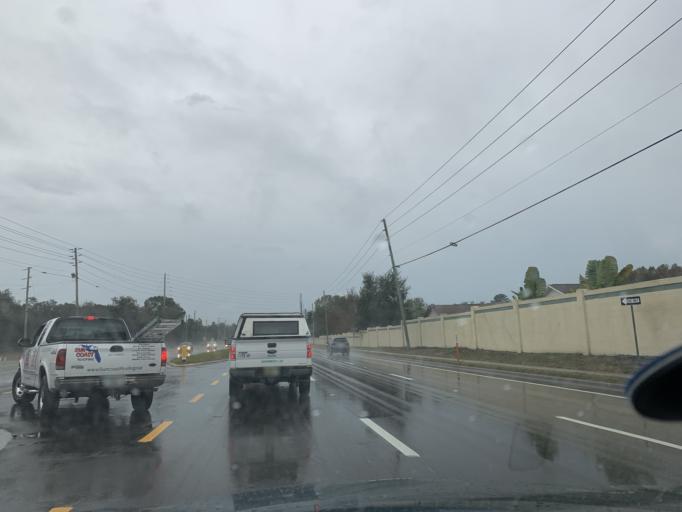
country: US
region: Florida
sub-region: Pasco County
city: Bayonet Point
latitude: 28.3113
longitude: -82.6662
